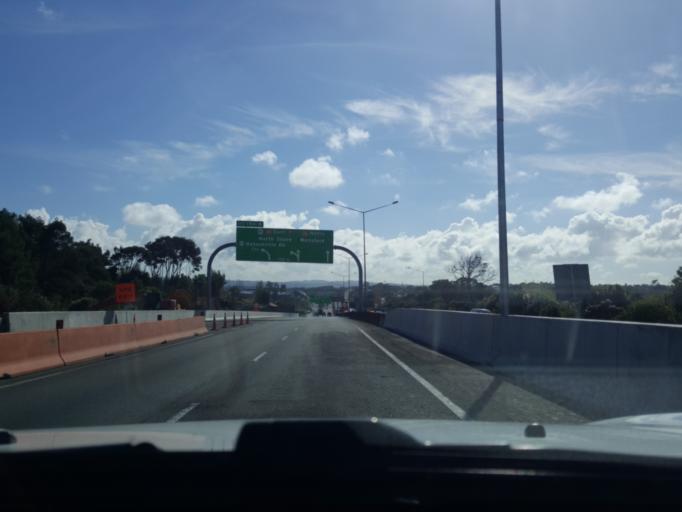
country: NZ
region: Auckland
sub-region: Auckland
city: Rosebank
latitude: -36.8300
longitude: 174.6188
